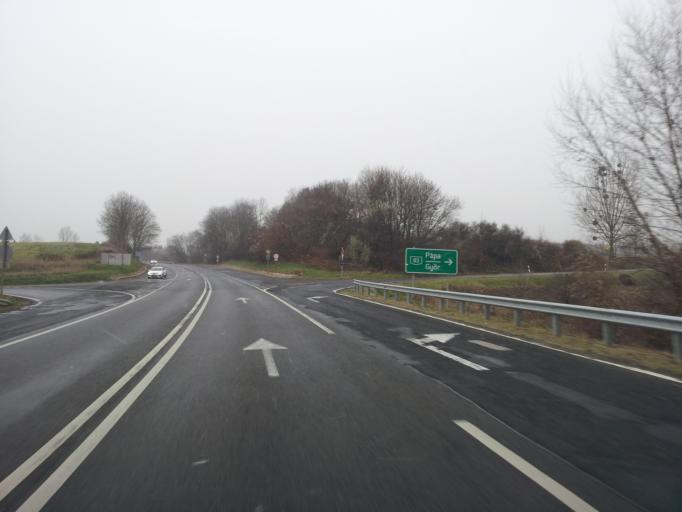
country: HU
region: Veszprem
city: Urkut
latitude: 47.1529
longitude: 17.6543
